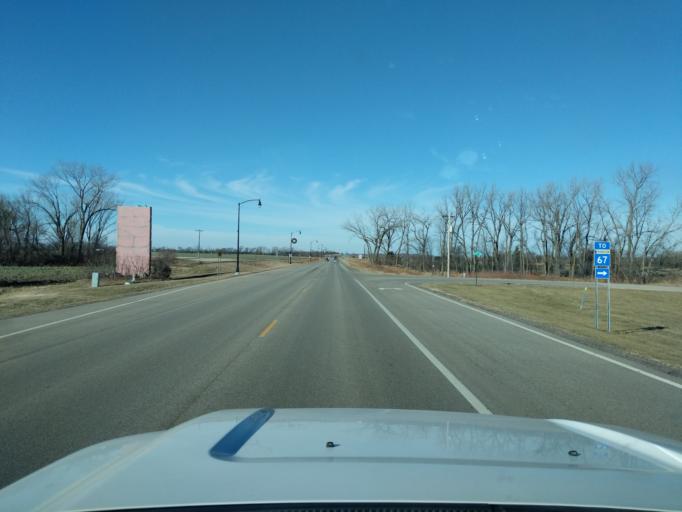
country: US
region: Minnesota
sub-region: Yellow Medicine County
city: Granite Falls
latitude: 44.7668
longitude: -95.5355
